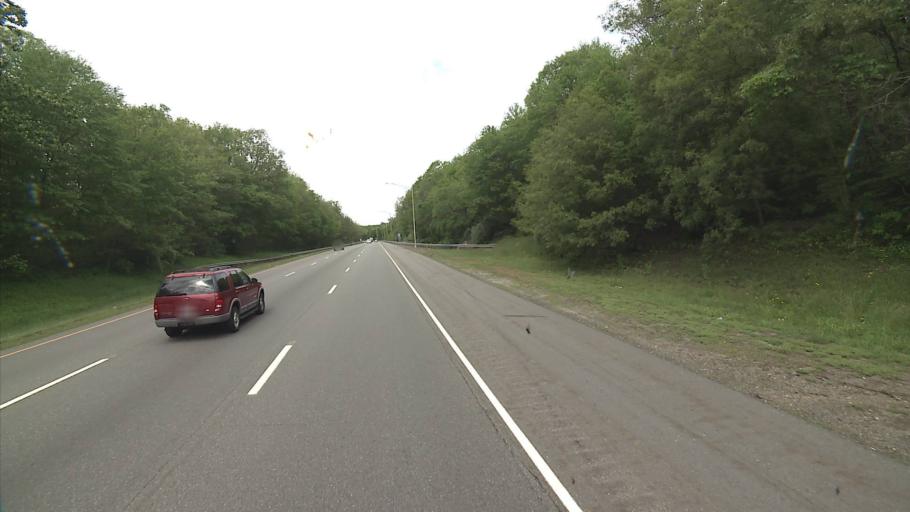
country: US
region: Connecticut
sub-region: New London County
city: Mystic
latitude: 41.3722
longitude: -71.9840
